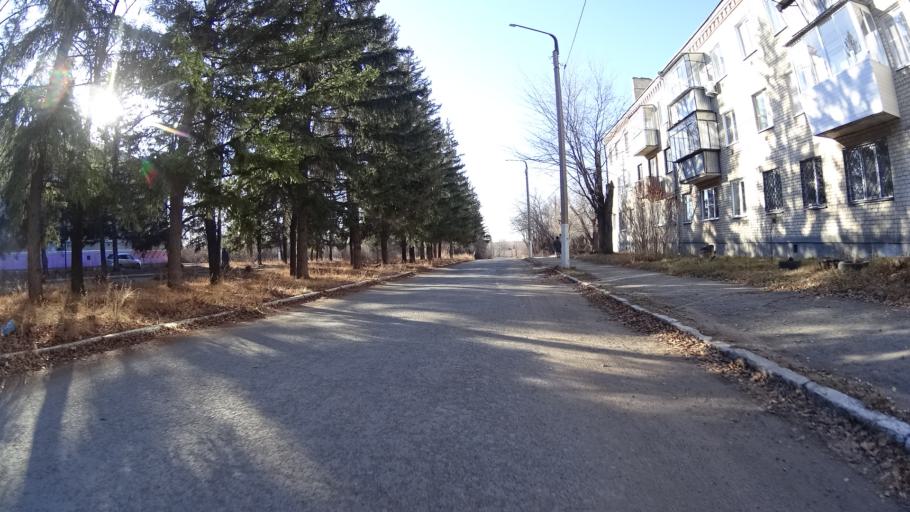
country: RU
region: Chelyabinsk
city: Troitsk
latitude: 54.0453
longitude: 61.6252
